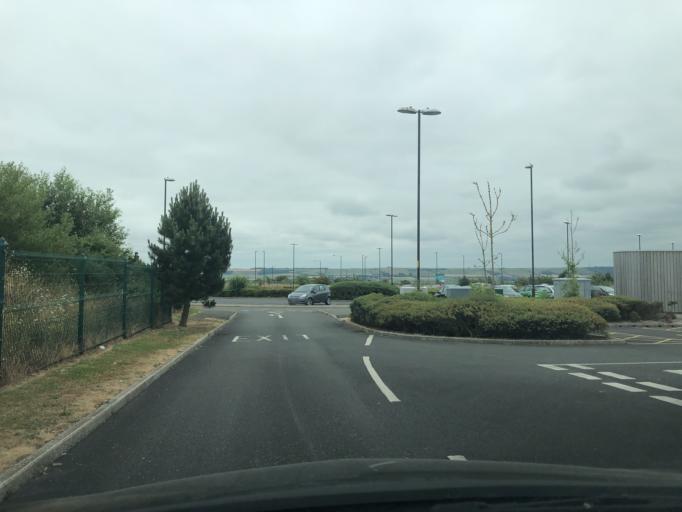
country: GB
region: England
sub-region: North Yorkshire
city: Scarborough
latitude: 54.2524
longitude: -0.3821
